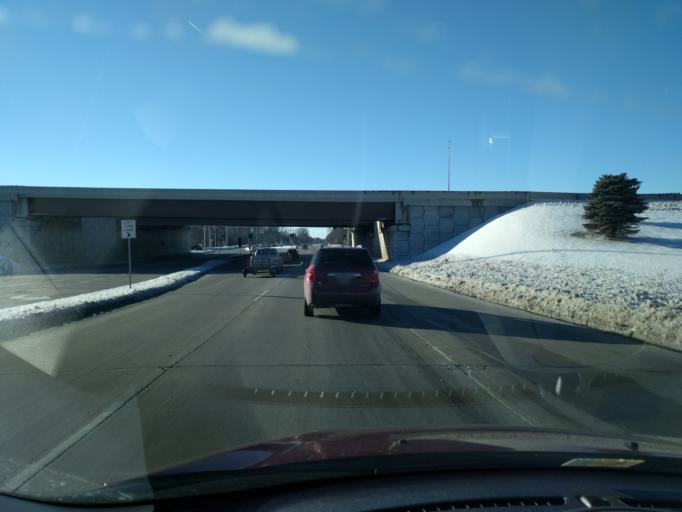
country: US
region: Wisconsin
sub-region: Milwaukee County
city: Whitefish Bay
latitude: 43.1191
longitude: -87.9177
